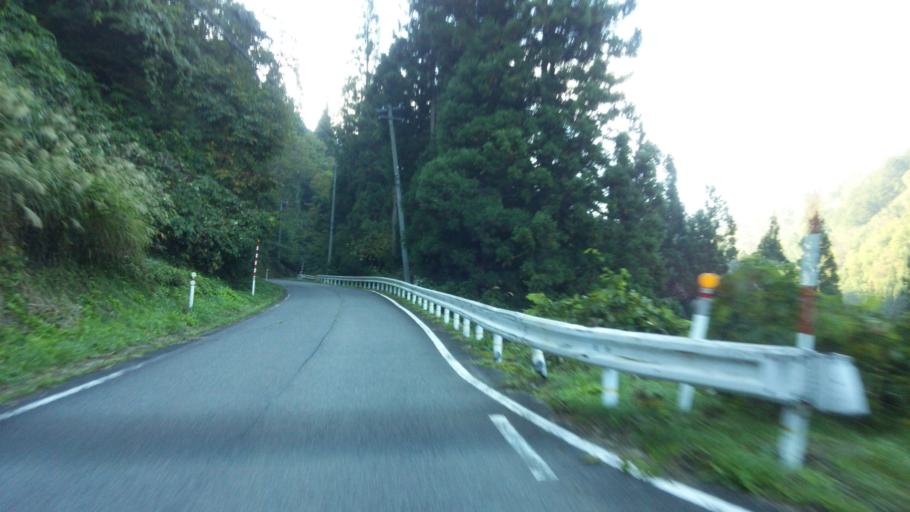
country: JP
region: Fukushima
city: Kitakata
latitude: 37.4264
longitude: 139.7257
